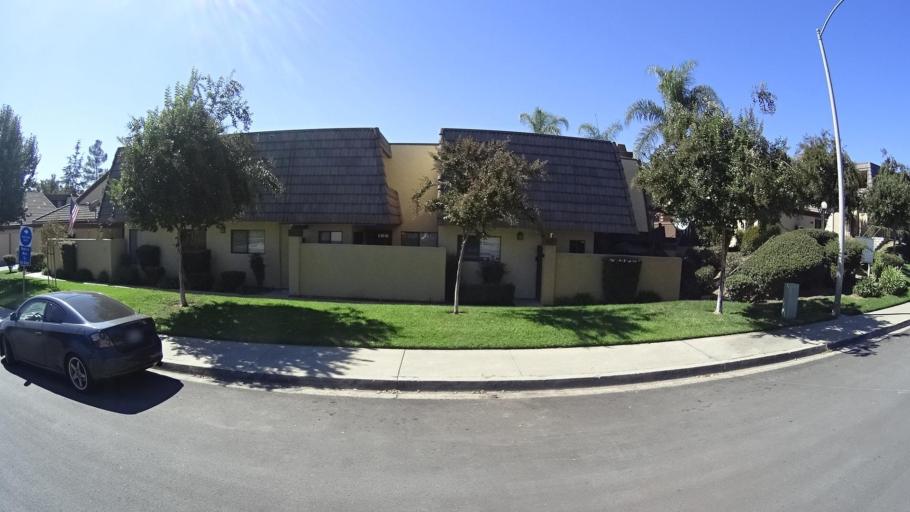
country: US
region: California
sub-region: San Diego County
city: Alpine
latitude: 32.8366
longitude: -116.7668
